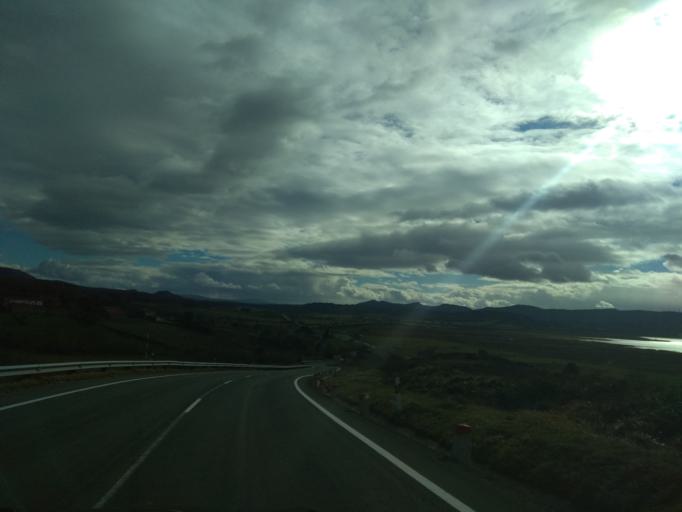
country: ES
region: Castille and Leon
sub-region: Provincia de Burgos
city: Arija
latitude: 43.0320
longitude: -3.8652
